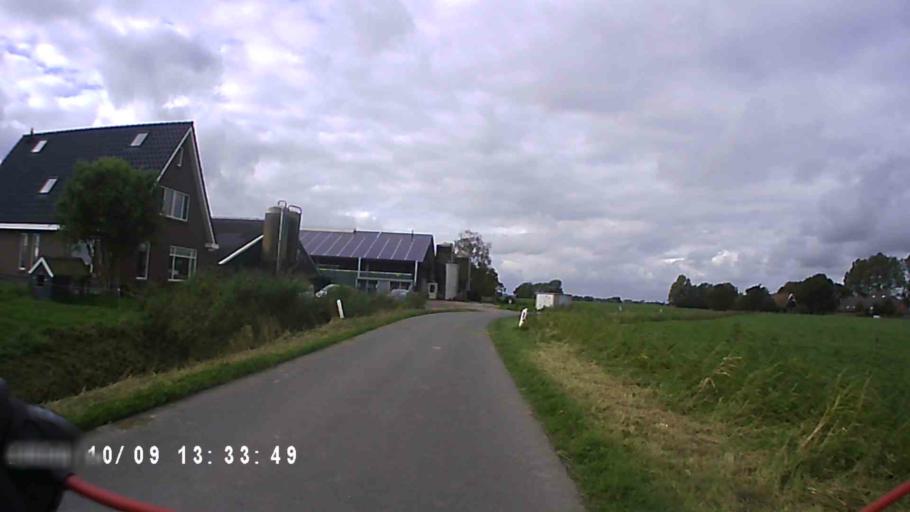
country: NL
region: Groningen
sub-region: Gemeente Zuidhorn
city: Aduard
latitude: 53.2904
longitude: 6.4714
